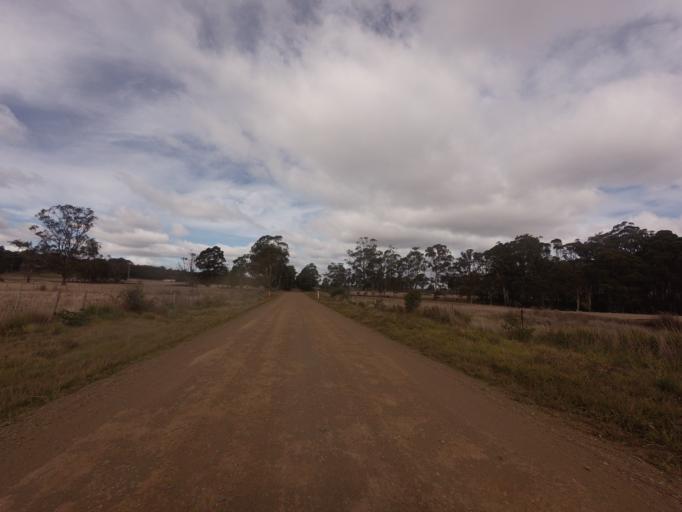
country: AU
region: Tasmania
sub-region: Brighton
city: Bridgewater
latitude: -42.4206
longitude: 147.4210
